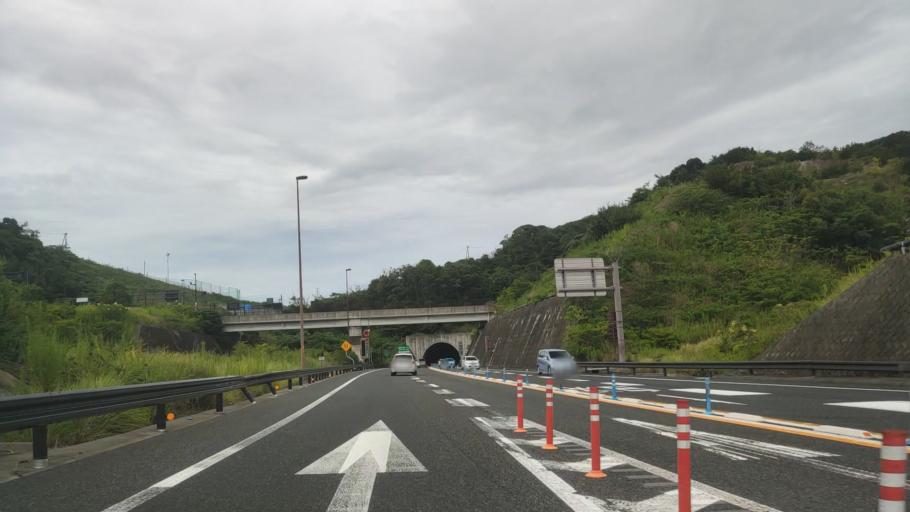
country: JP
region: Wakayama
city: Tanabe
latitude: 33.7460
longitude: 135.3700
